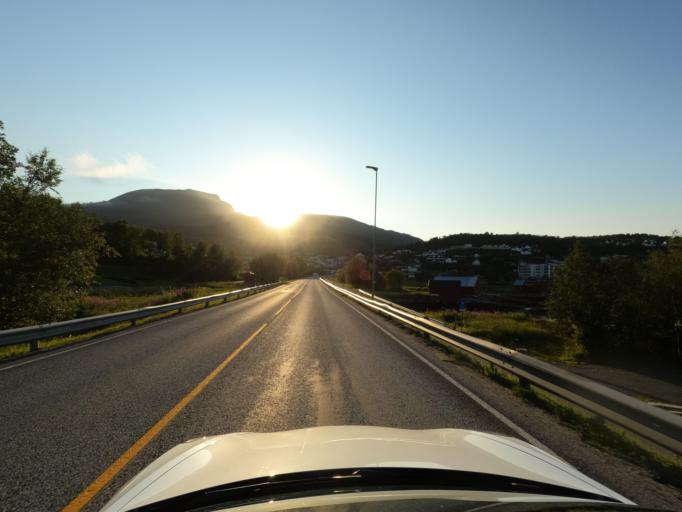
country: NO
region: Troms
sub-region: Harstad
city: Harstad
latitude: 68.7447
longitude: 16.5636
